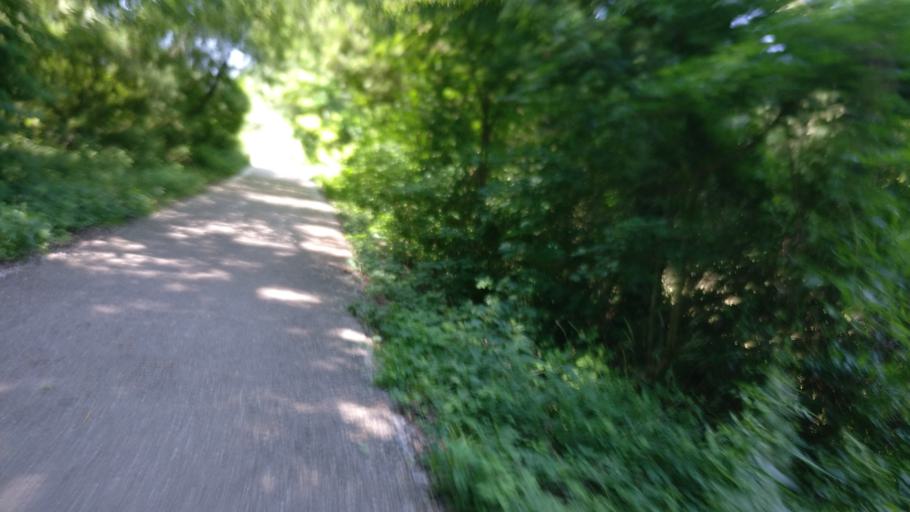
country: AT
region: Lower Austria
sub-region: Politischer Bezirk Baden
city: Gunselsdorf
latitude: 47.9473
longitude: 16.2657
